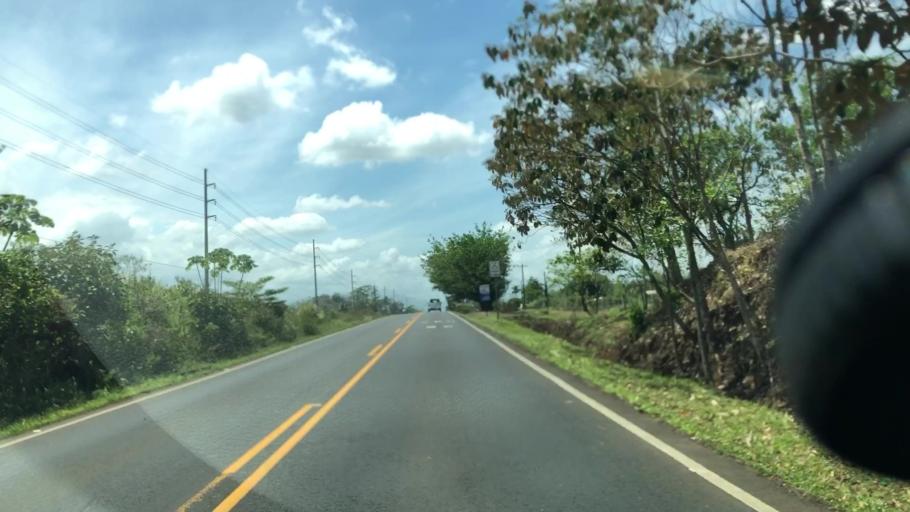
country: CR
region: Alajuela
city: Pital
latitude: 10.4570
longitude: -84.4040
